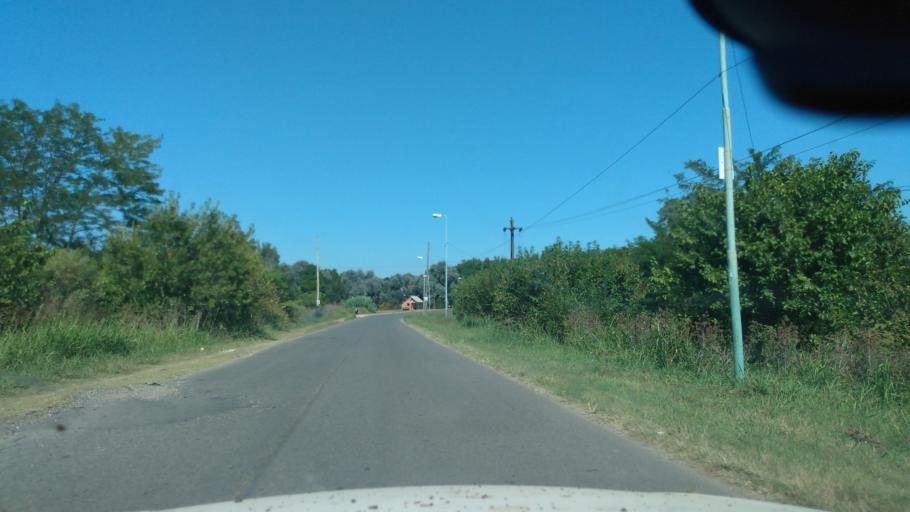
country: AR
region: Buenos Aires
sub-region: Partido de Lujan
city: Lujan
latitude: -34.5088
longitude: -59.0847
